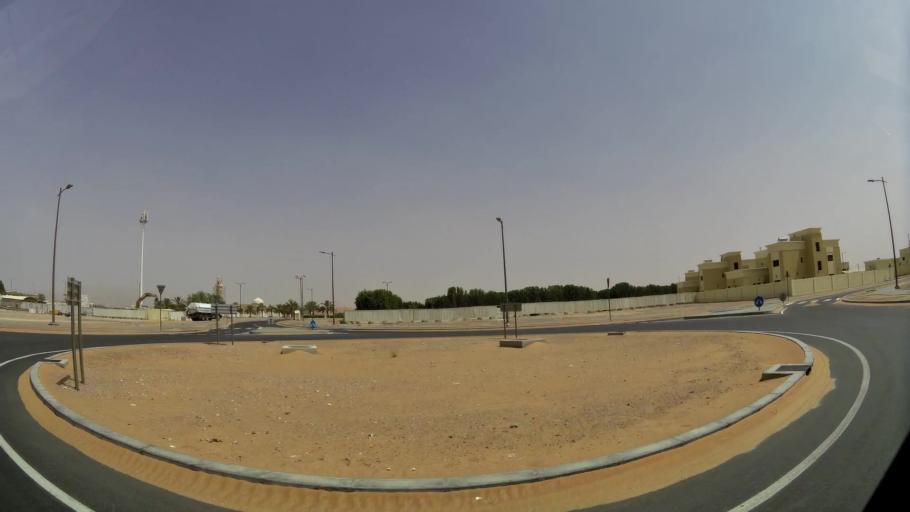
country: AE
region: Abu Dhabi
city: Al Ain
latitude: 24.1380
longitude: 55.6315
